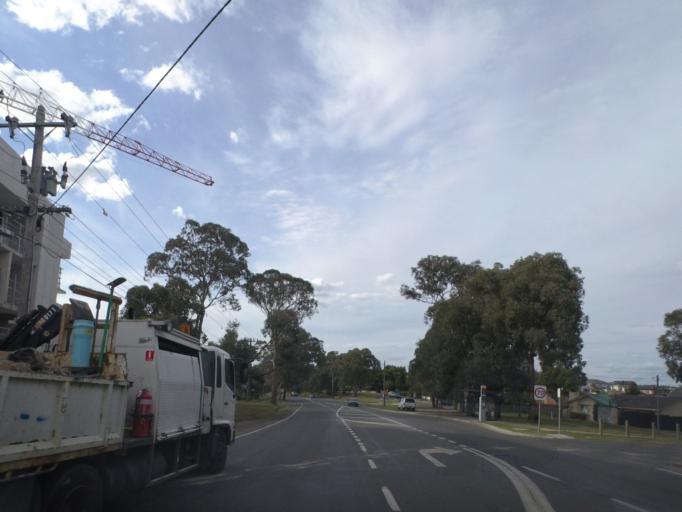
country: AU
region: Victoria
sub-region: Manningham
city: Donvale
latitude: -37.7628
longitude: 145.1733
